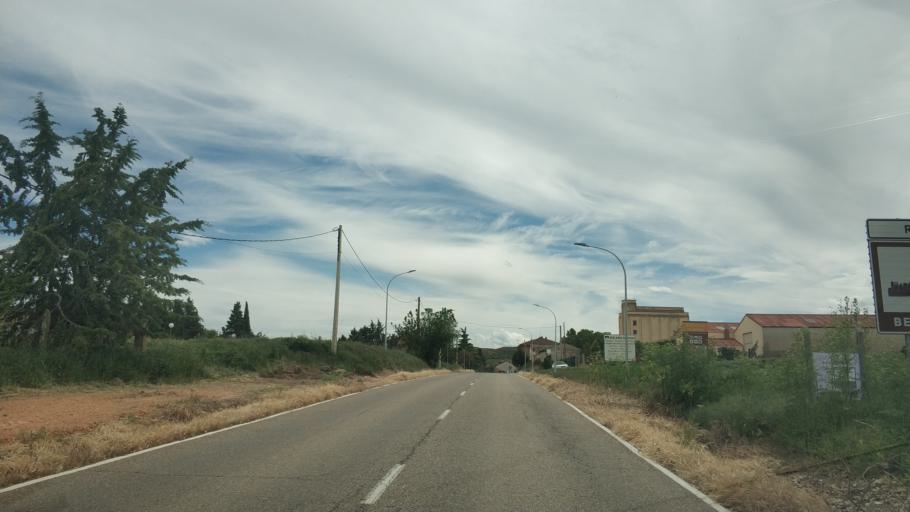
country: ES
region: Castille and Leon
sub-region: Provincia de Soria
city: Berlanga de Duero
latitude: 41.4711
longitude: -2.8616
